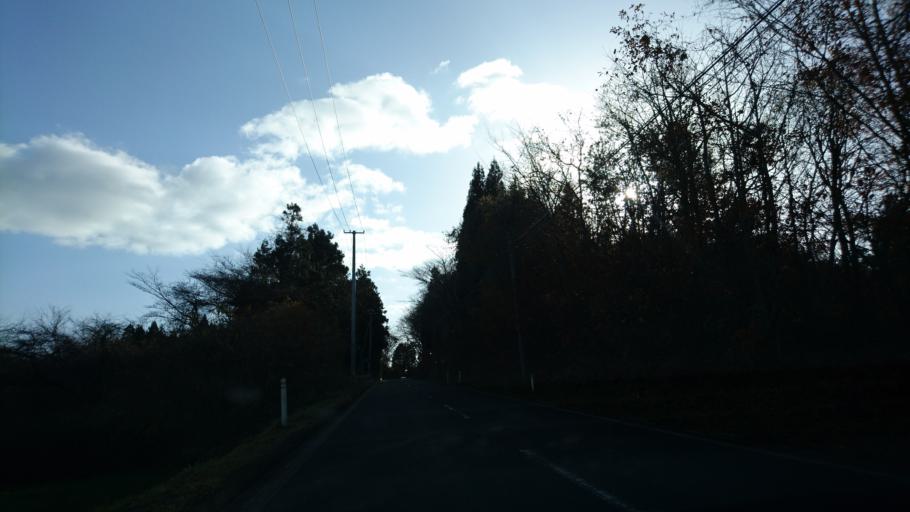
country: JP
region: Iwate
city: Ichinoseki
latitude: 38.8869
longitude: 141.2899
